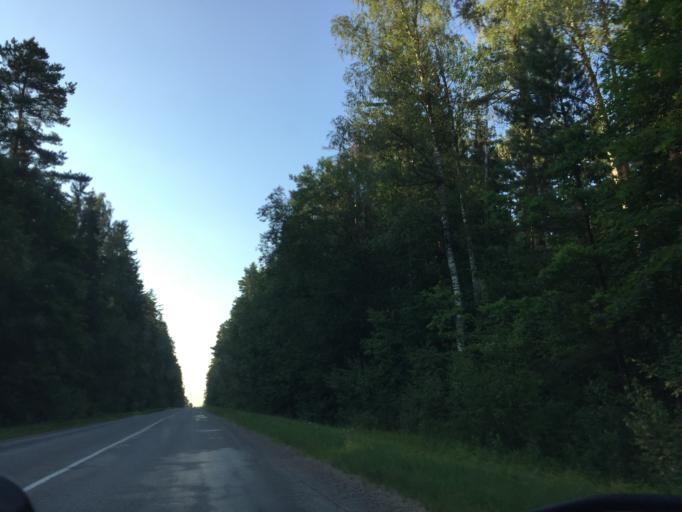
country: LV
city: Tervete
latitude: 56.4613
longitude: 23.4050
